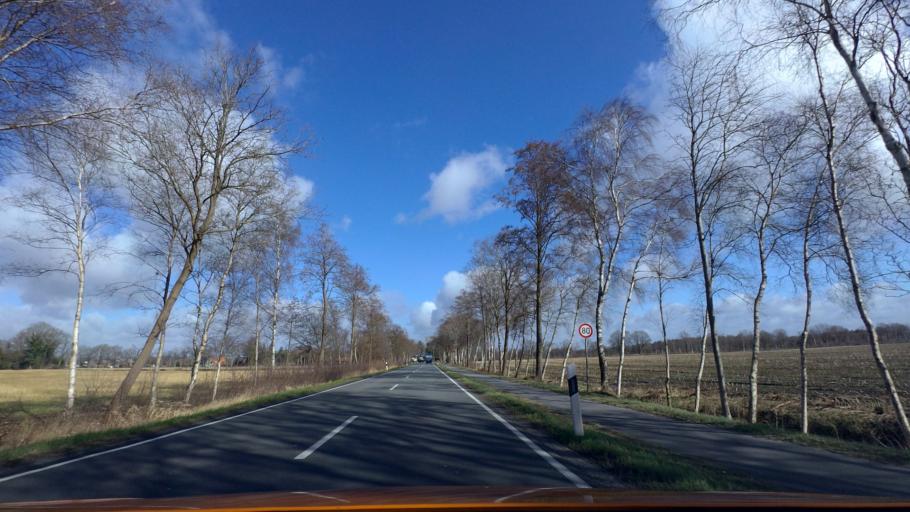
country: DE
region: Lower Saxony
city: Edewecht
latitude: 53.0973
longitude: 7.9485
